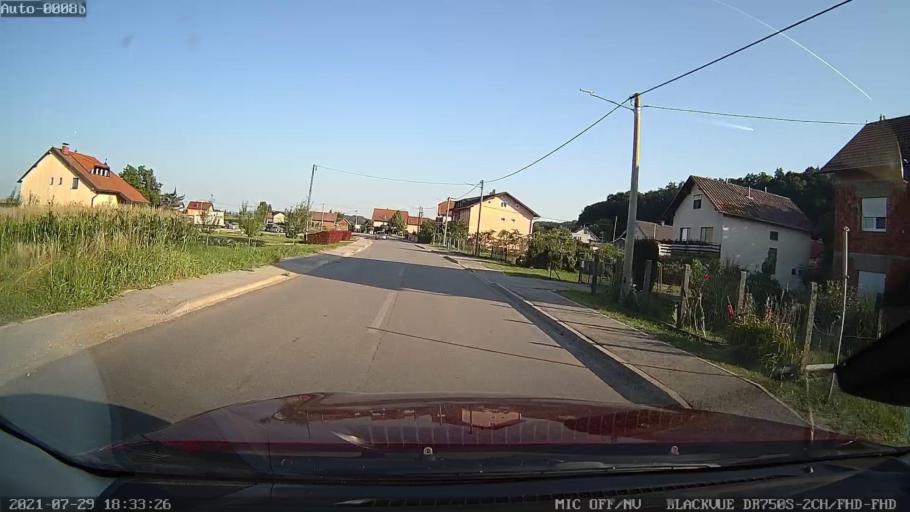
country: HR
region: Varazdinska
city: Vinica
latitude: 46.3160
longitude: 16.1582
